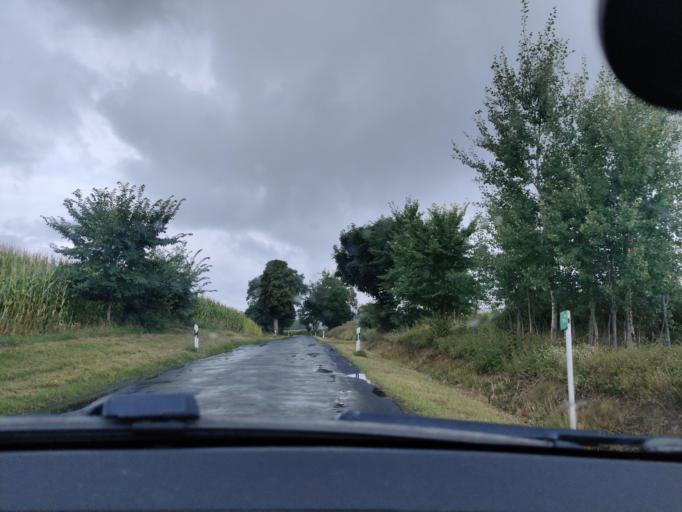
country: DE
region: Mecklenburg-Vorpommern
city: Wesenberg
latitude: 53.2705
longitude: 13.0016
